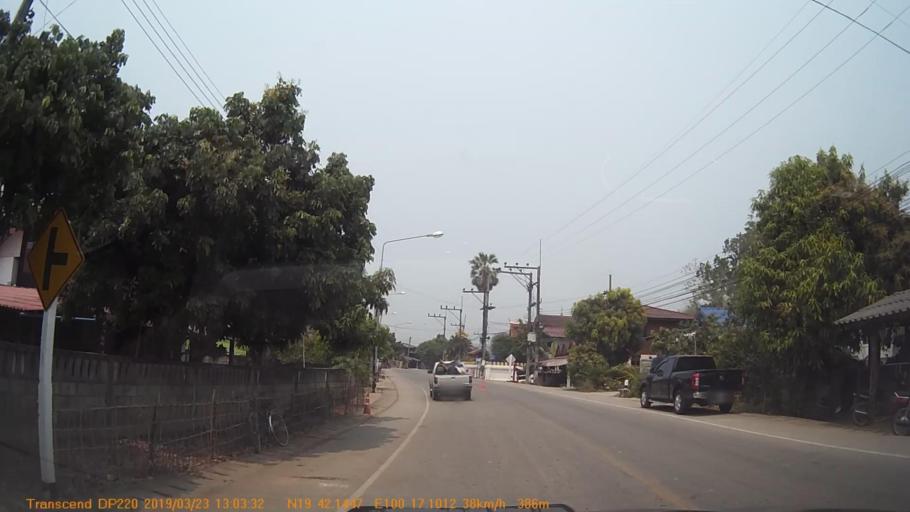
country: TH
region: Chiang Rai
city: Thoeng
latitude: 19.7026
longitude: 100.2851
